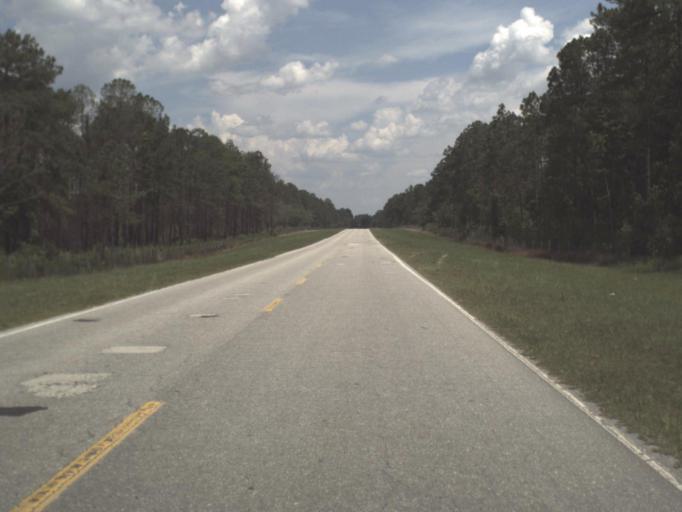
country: US
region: Florida
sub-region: Bradford County
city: Starke
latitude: 29.9889
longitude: -82.0212
